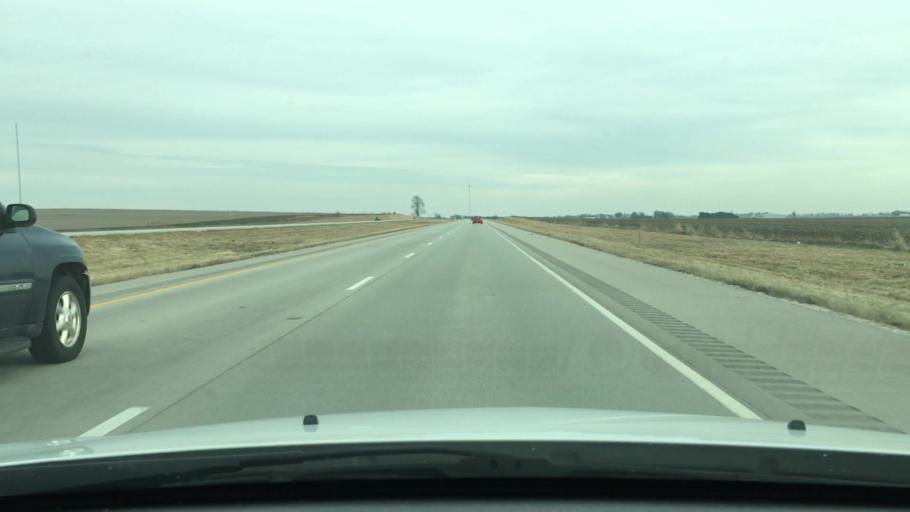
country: US
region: Illinois
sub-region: Morgan County
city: Jacksonville
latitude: 39.7376
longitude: -90.1020
